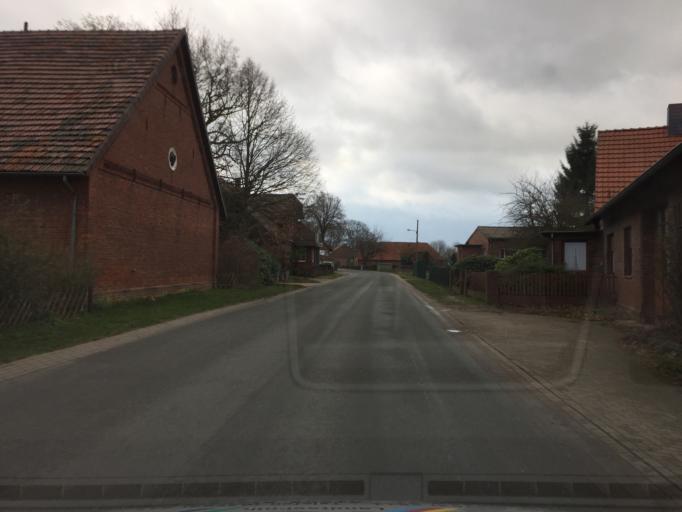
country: DE
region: Lower Saxony
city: Stolzenau
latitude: 52.5221
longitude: 9.0563
